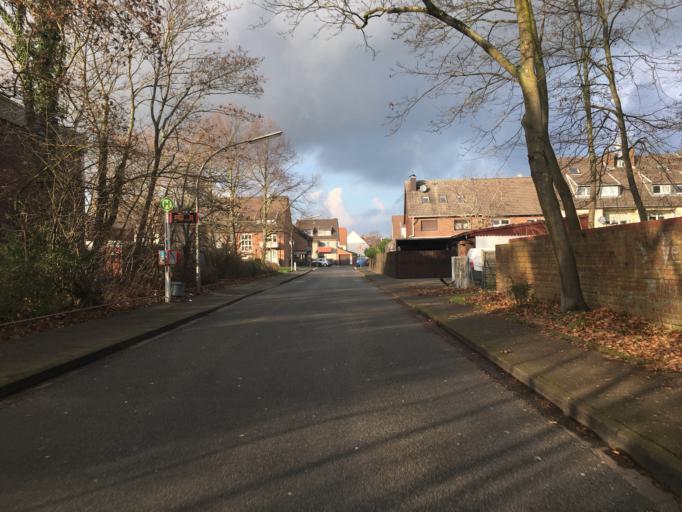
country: DE
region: North Rhine-Westphalia
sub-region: Regierungsbezirk Dusseldorf
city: Dormagen
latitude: 51.0613
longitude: 6.8566
